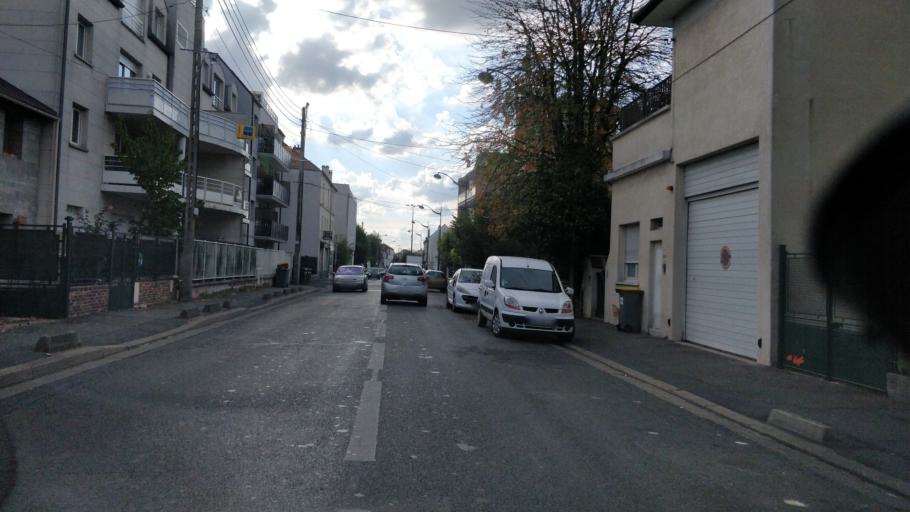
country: FR
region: Ile-de-France
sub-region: Departement de Seine-Saint-Denis
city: Gagny
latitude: 48.8976
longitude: 2.5336
